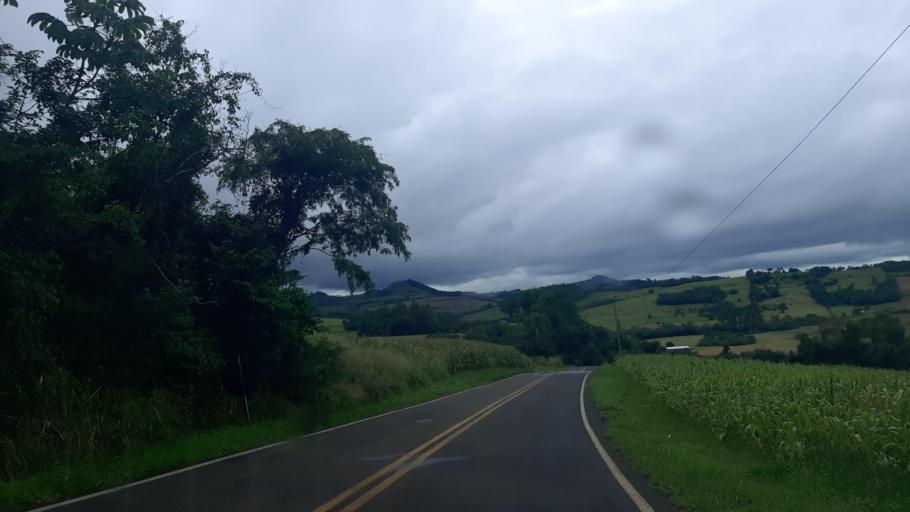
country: BR
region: Parana
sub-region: Ampere
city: Ampere
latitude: -25.9917
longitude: -53.4385
